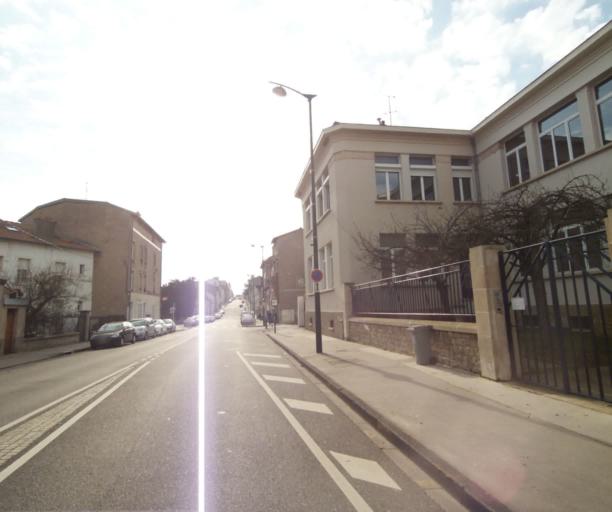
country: FR
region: Lorraine
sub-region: Departement de Meurthe-et-Moselle
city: Laxou
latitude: 48.6825
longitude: 6.1557
